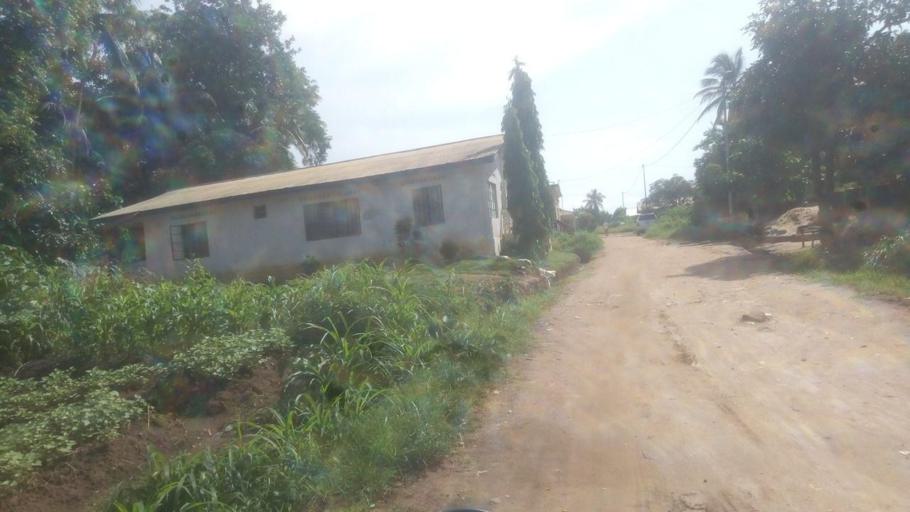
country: SL
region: Northern Province
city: Masoyila
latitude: 8.6090
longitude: -13.1961
